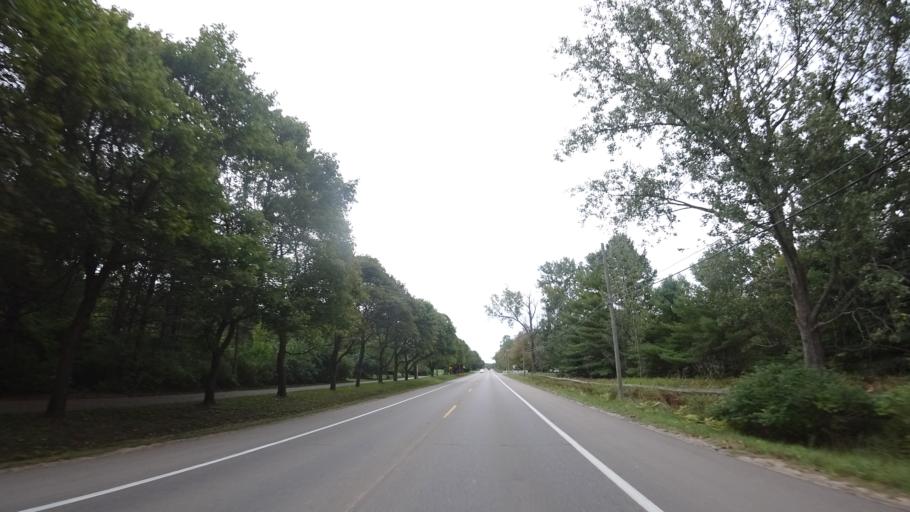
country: US
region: Michigan
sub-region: Emmet County
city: Harbor Springs
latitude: 45.4315
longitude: -84.9526
